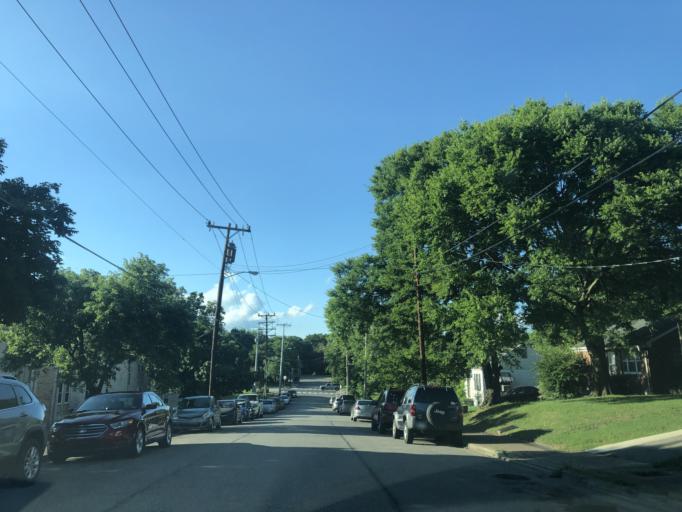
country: US
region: Tennessee
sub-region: Davidson County
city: Nashville
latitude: 36.1834
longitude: -86.7584
